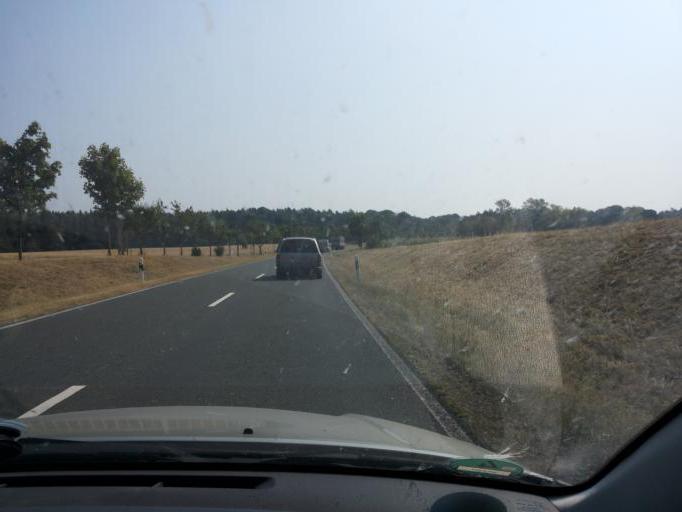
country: DE
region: Bavaria
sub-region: Regierungsbezirk Mittelfranken
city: Ipsheim
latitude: 49.5045
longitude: 10.5222
